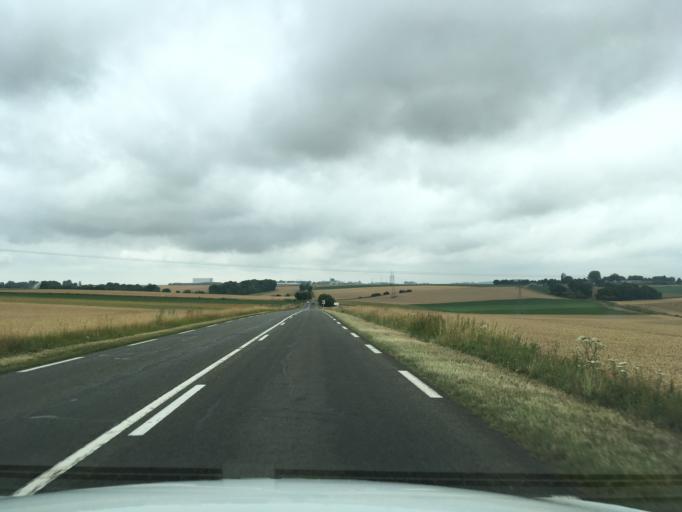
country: FR
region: Picardie
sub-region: Departement de l'Aisne
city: Vermand
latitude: 49.8786
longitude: 3.0849
